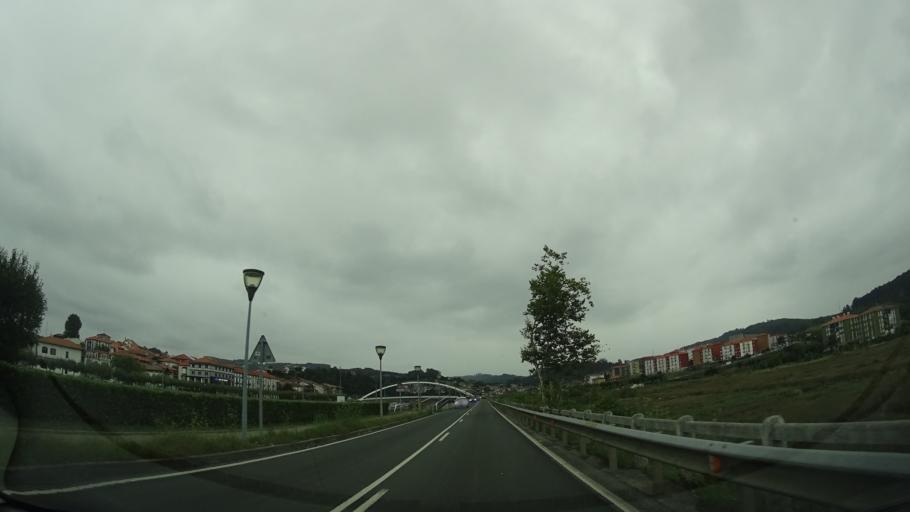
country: ES
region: Basque Country
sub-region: Bizkaia
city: Plentzia
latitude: 43.4036
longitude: -2.9522
